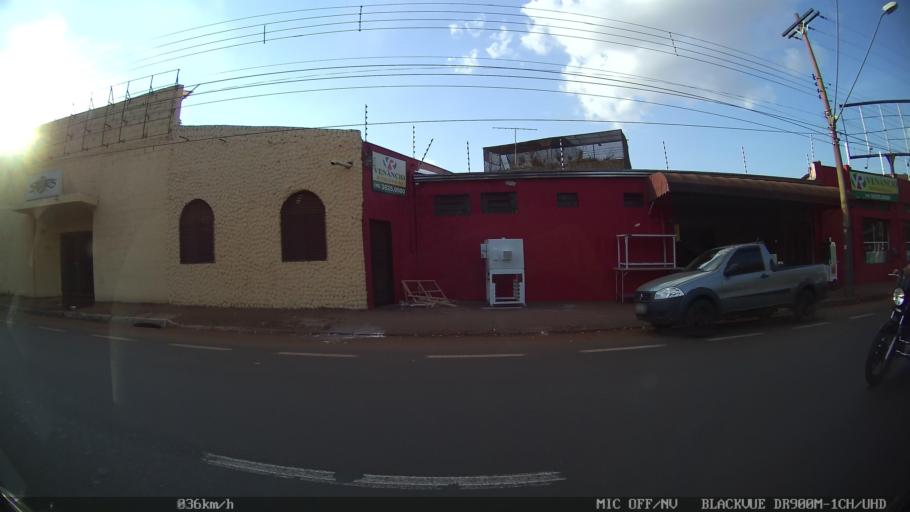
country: BR
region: Sao Paulo
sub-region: Ribeirao Preto
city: Ribeirao Preto
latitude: -21.1657
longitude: -47.8143
